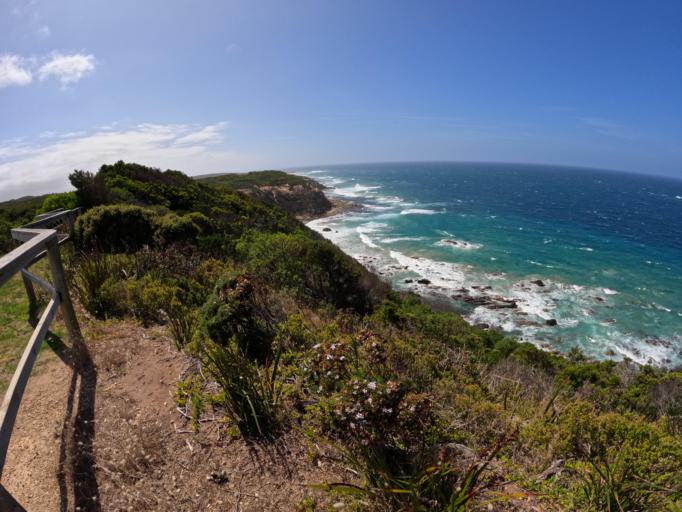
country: AU
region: Victoria
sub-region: Colac-Otway
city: Apollo Bay
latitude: -38.8554
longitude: 143.5153
